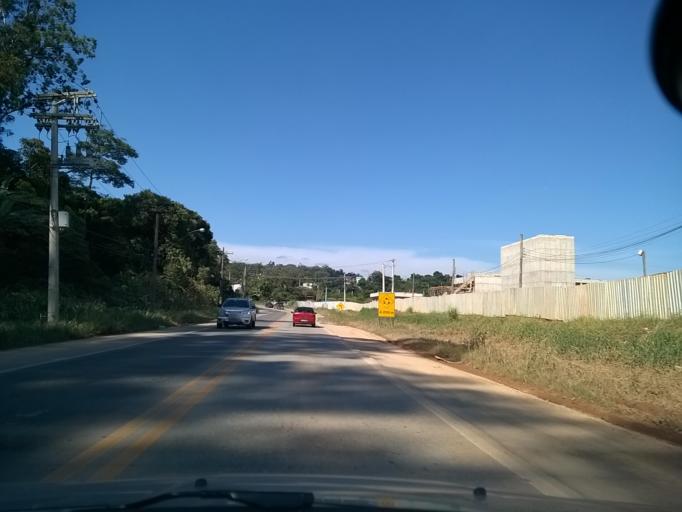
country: BR
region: Sao Paulo
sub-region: Caieiras
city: Caieiras
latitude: -23.3568
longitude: -46.7455
